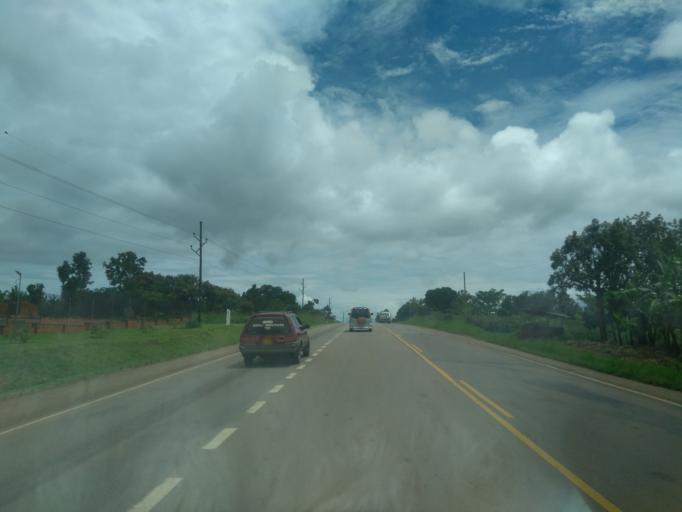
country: UG
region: Central Region
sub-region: Butambala District
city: Gombe
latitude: 0.0056
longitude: 32.0450
